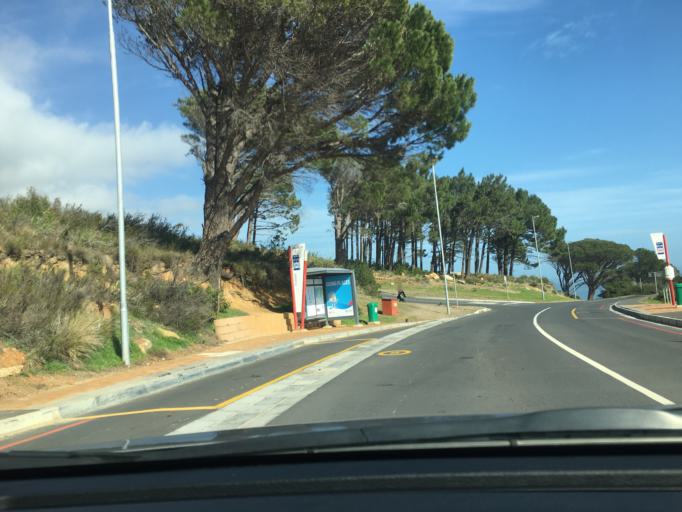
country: ZA
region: Western Cape
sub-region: City of Cape Town
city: Cape Town
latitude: -33.9585
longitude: 18.3833
